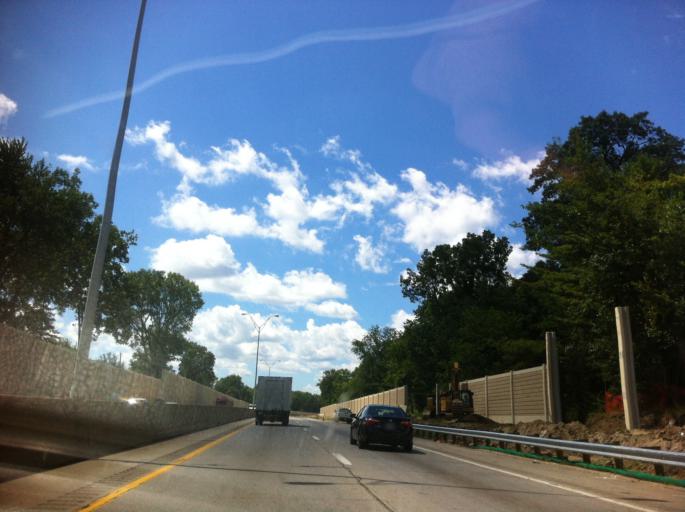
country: US
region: Ohio
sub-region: Lucas County
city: Ottawa Hills
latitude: 41.6880
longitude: -83.6469
